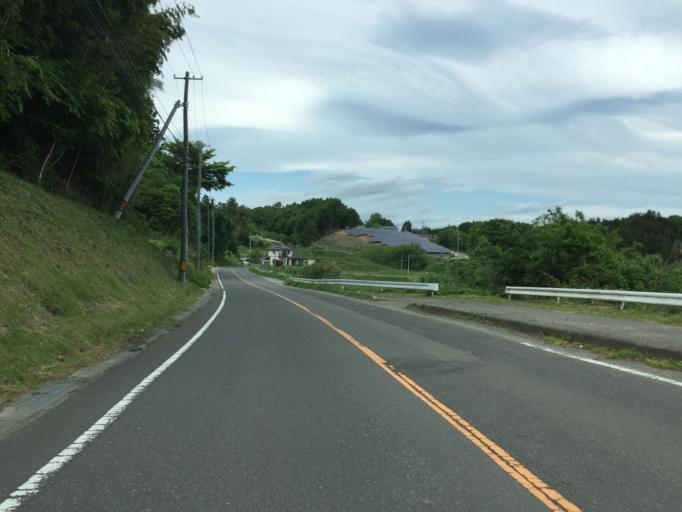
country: JP
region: Fukushima
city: Nihommatsu
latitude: 37.6348
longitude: 140.4925
